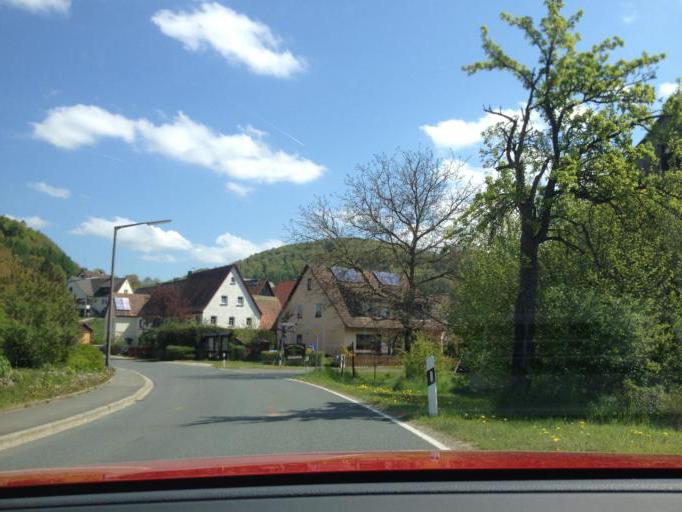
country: DE
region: Bavaria
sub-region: Regierungsbezirk Mittelfranken
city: Simmelsdorf
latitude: 49.5869
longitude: 11.3635
